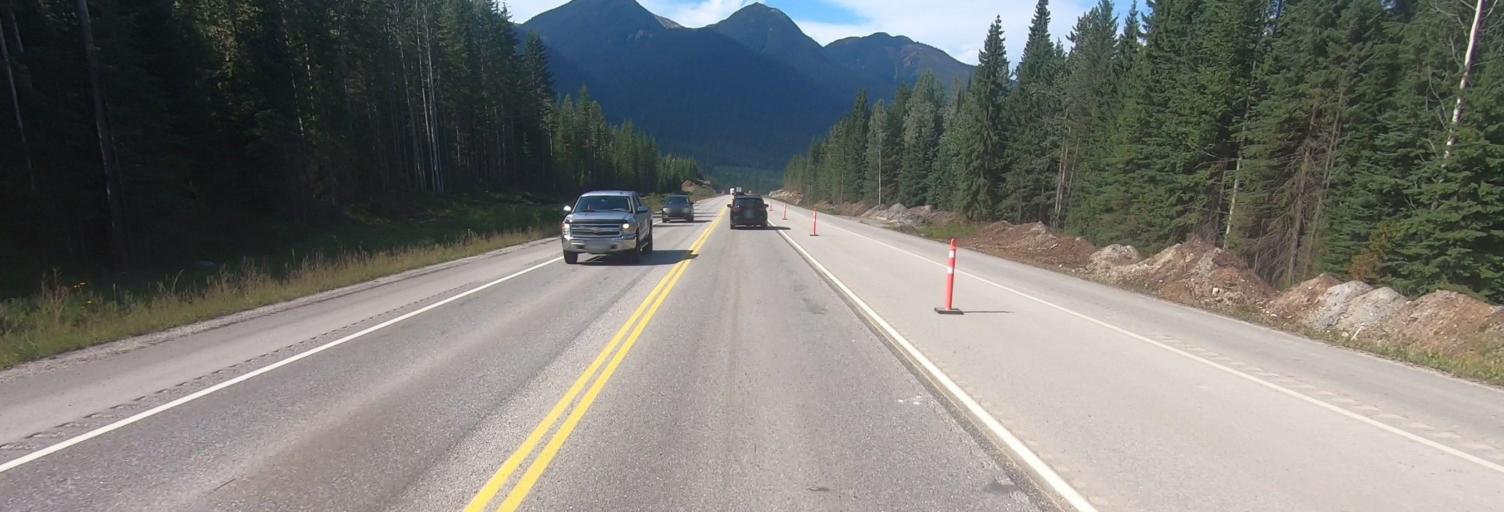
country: CA
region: British Columbia
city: Golden
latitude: 51.4816
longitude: -117.3430
